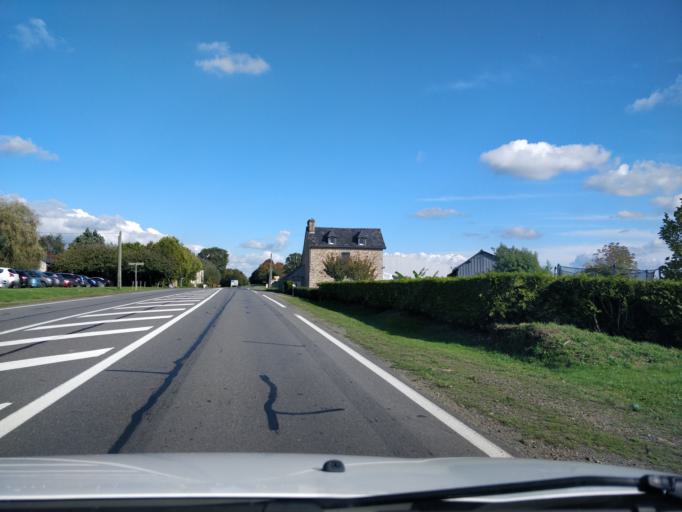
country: FR
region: Brittany
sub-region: Departement d'Ille-et-Vilaine
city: Saint-Aubin-du-Cormier
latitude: 48.2556
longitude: -1.4187
